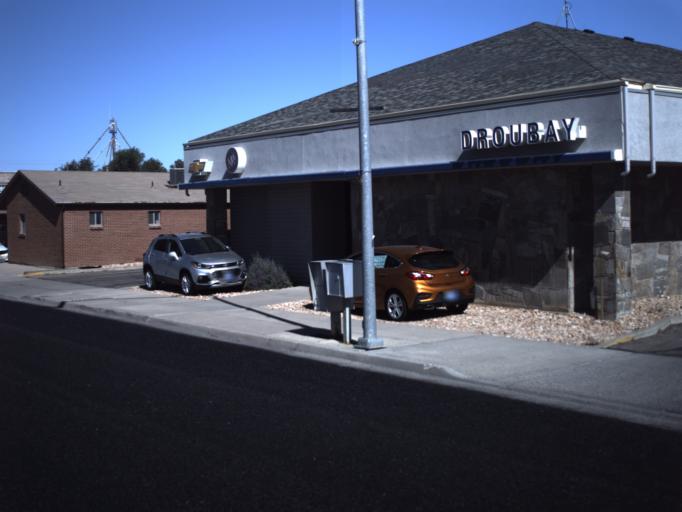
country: US
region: Utah
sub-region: Millard County
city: Delta
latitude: 39.3525
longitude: -112.5823
